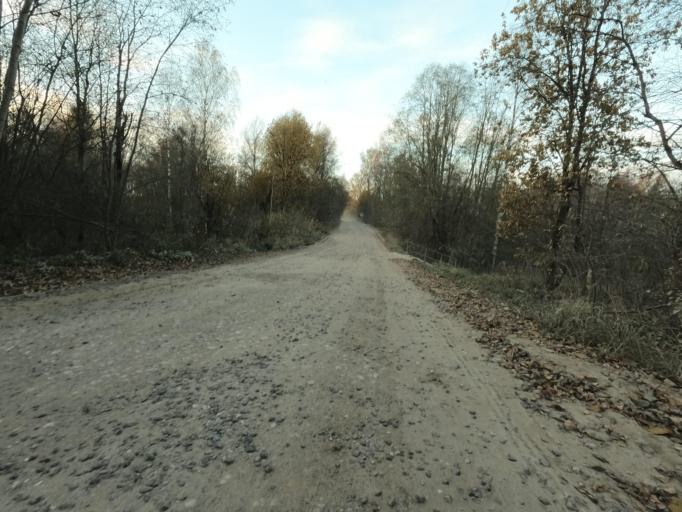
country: RU
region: Leningrad
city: Mga
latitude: 59.7729
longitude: 31.2263
